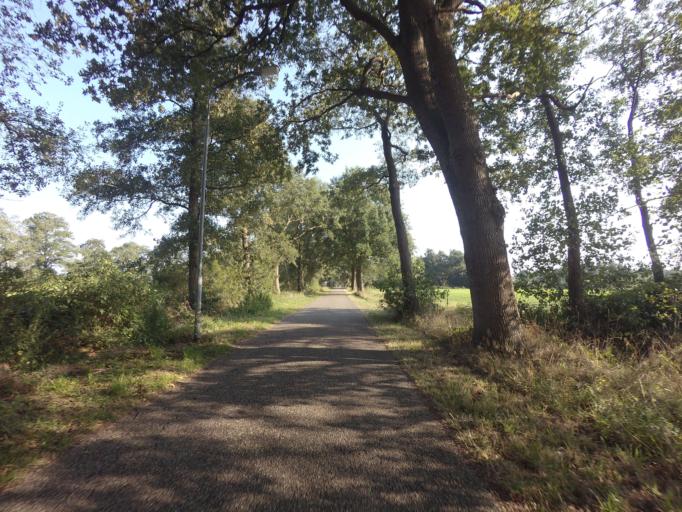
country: NL
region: Drenthe
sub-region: Gemeente Tynaarlo
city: Vries
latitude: 53.1300
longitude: 6.4904
